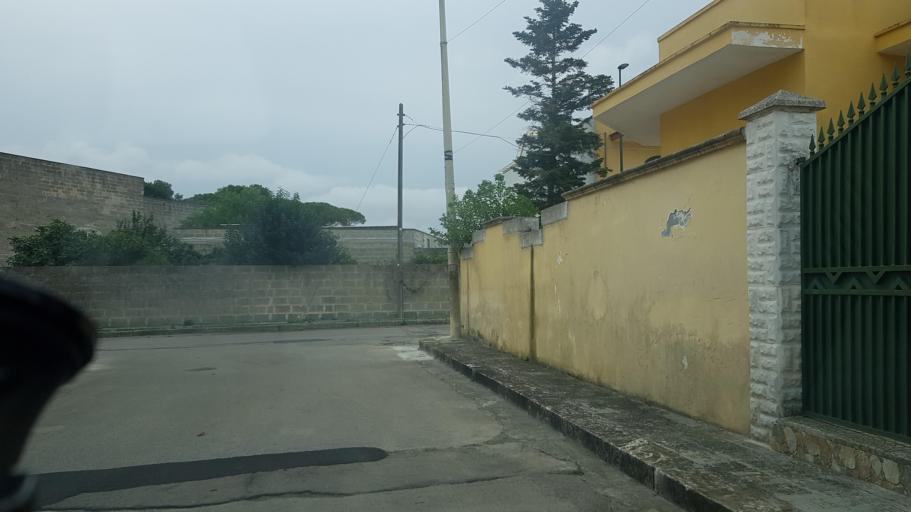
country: IT
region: Apulia
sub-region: Provincia di Lecce
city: Guagnano
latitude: 40.4047
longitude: 17.9498
